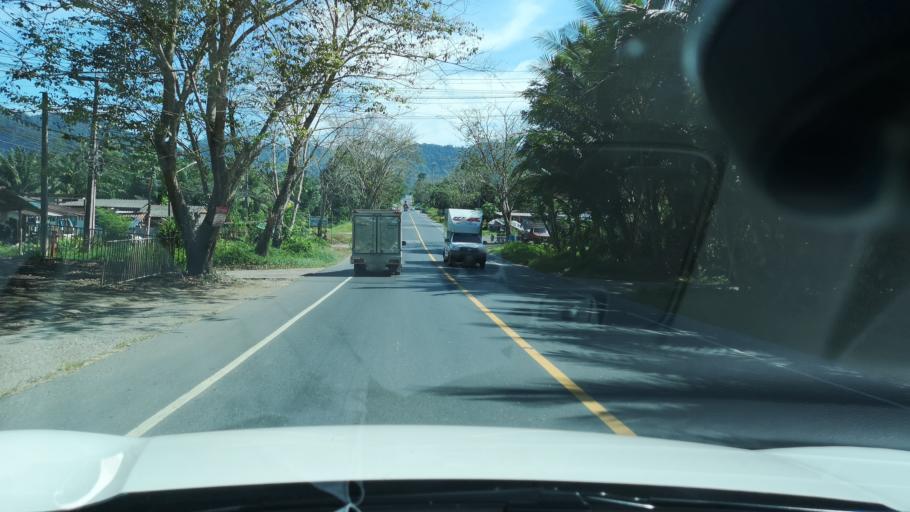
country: TH
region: Phangnga
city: Phang Nga
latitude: 8.5324
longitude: 98.5146
